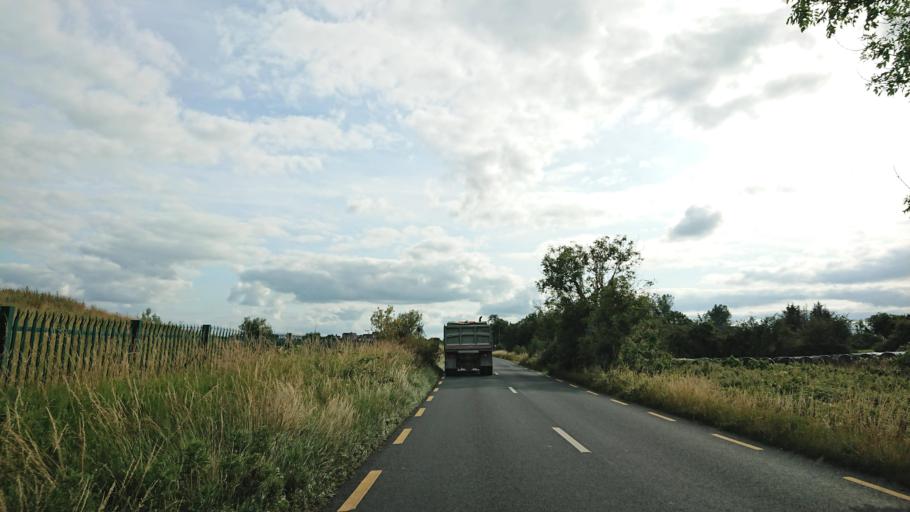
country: IE
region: Connaught
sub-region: County Leitrim
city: Carrick-on-Shannon
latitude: 53.9592
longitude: -8.0794
